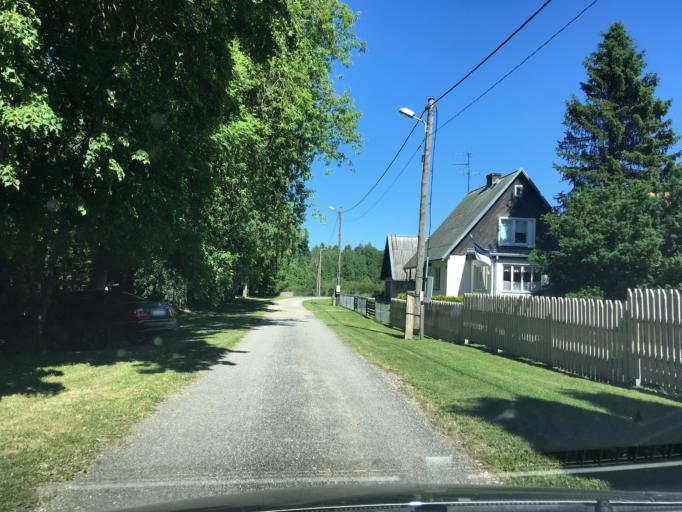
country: EE
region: Harju
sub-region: Raasiku vald
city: Raasiku
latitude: 59.1840
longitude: 25.1784
